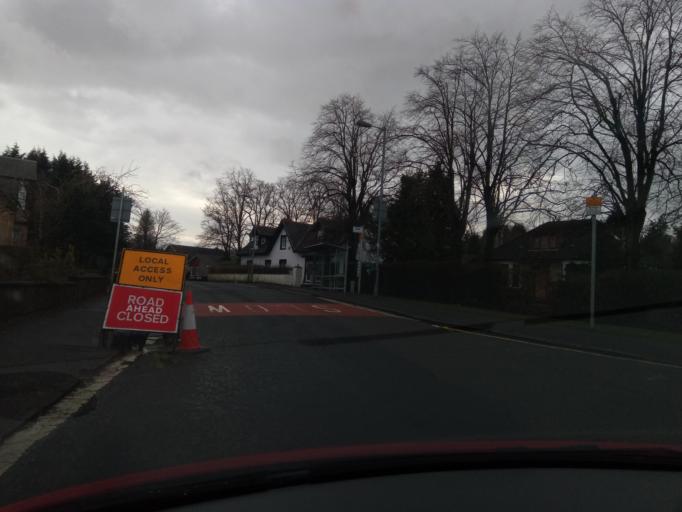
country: GB
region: Scotland
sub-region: East Dunbartonshire
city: Kirkintilloch
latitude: 55.9253
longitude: -4.1568
